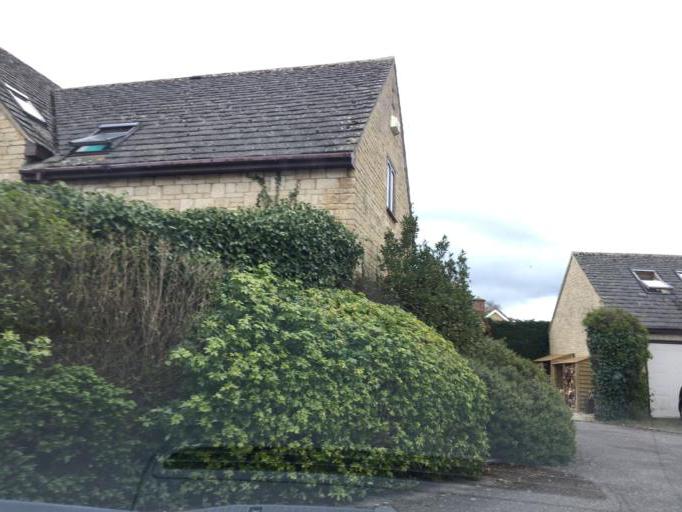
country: GB
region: England
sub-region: Oxfordshire
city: Stonesfield
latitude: 51.8533
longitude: -1.4285
